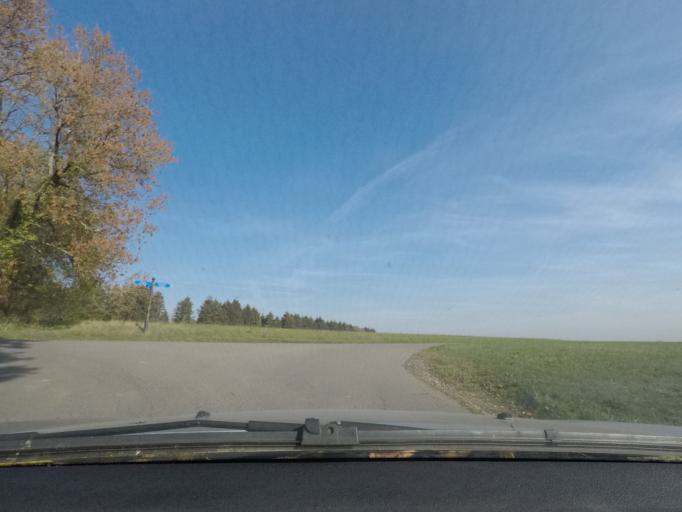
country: BE
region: Wallonia
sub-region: Province du Luxembourg
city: Tintigny
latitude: 49.6951
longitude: 5.4605
